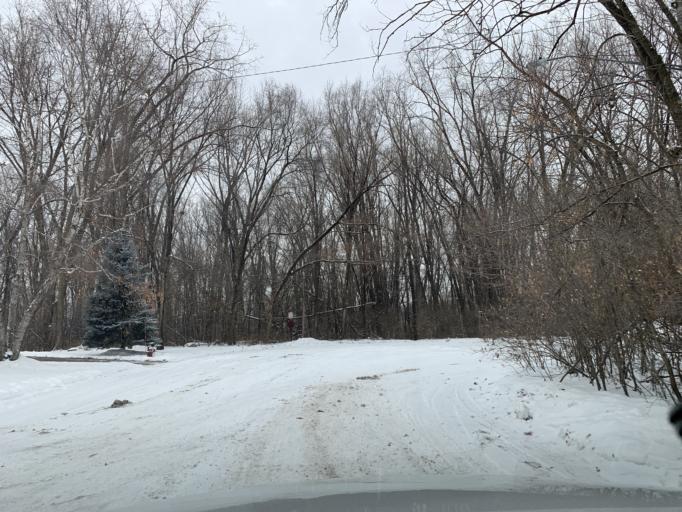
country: US
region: Minnesota
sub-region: Hennepin County
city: Edina
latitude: 44.9180
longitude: -93.3580
